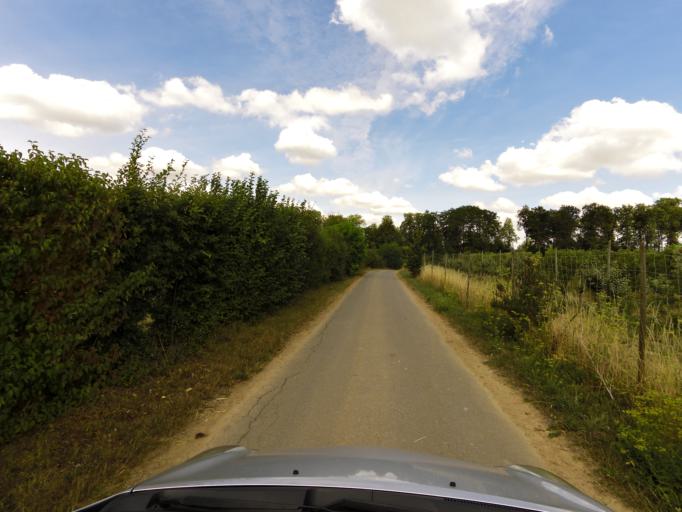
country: FR
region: Picardie
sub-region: Departement de l'Aisne
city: Villers-Cotterets
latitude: 49.2477
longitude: 3.1560
